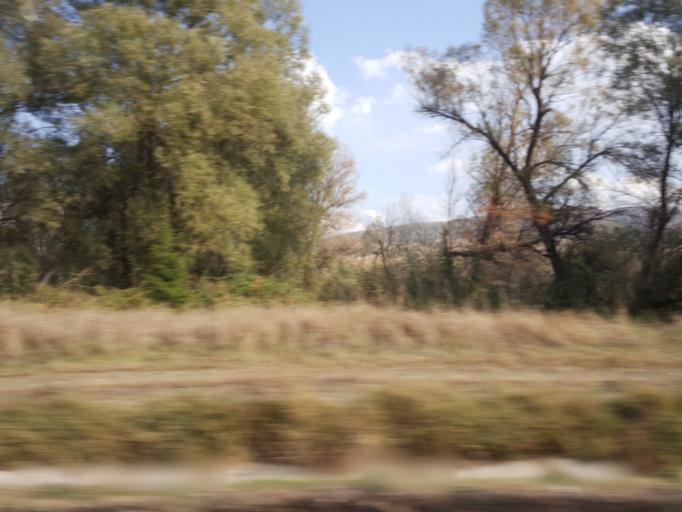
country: TR
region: Corum
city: Seydim
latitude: 40.3971
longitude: 34.7226
